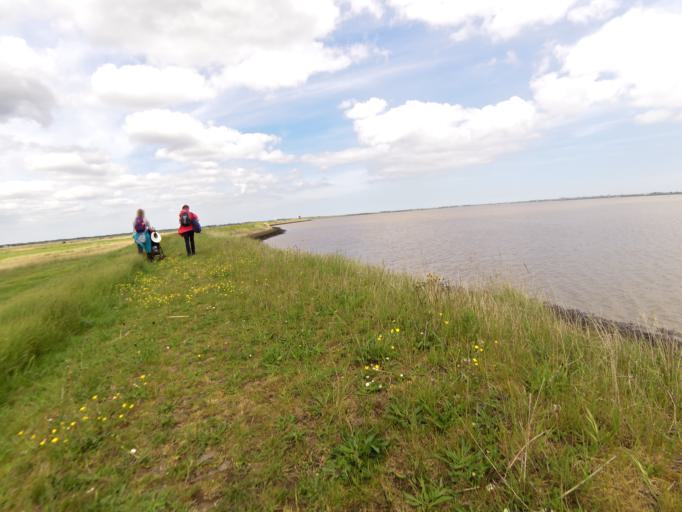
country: GB
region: England
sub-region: Norfolk
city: Great Yarmouth
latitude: 52.5985
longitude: 1.6532
